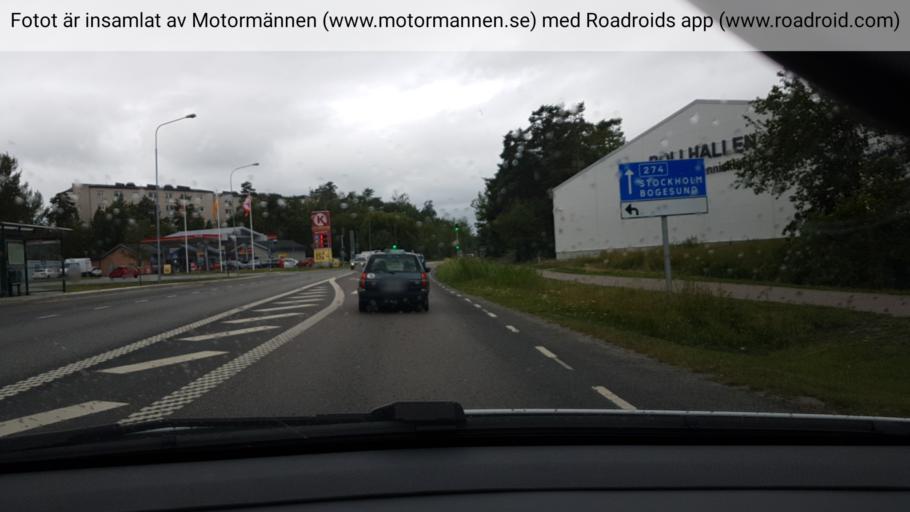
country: SE
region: Stockholm
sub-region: Vaxholms Kommun
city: Vaxholm
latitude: 59.4031
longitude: 18.3278
